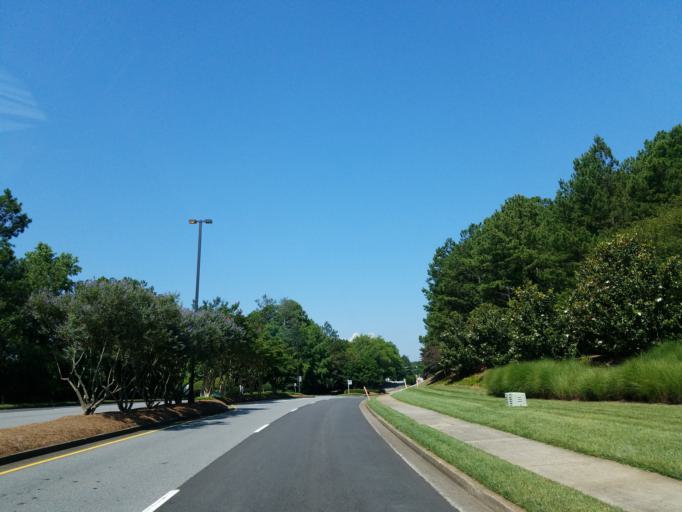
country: US
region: Georgia
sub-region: Fulton County
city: Alpharetta
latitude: 34.0551
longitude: -84.2721
